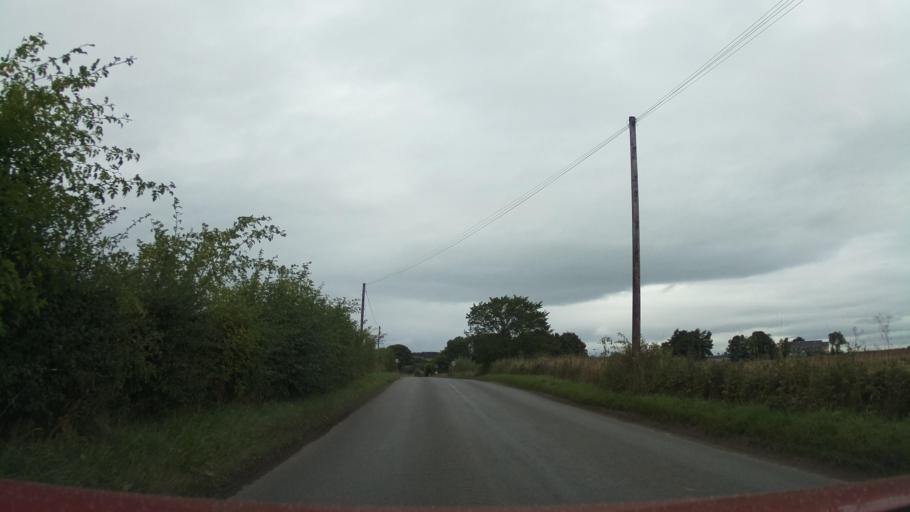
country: GB
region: Scotland
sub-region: Perth and Kinross
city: Milnathort
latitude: 56.2339
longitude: -3.3642
